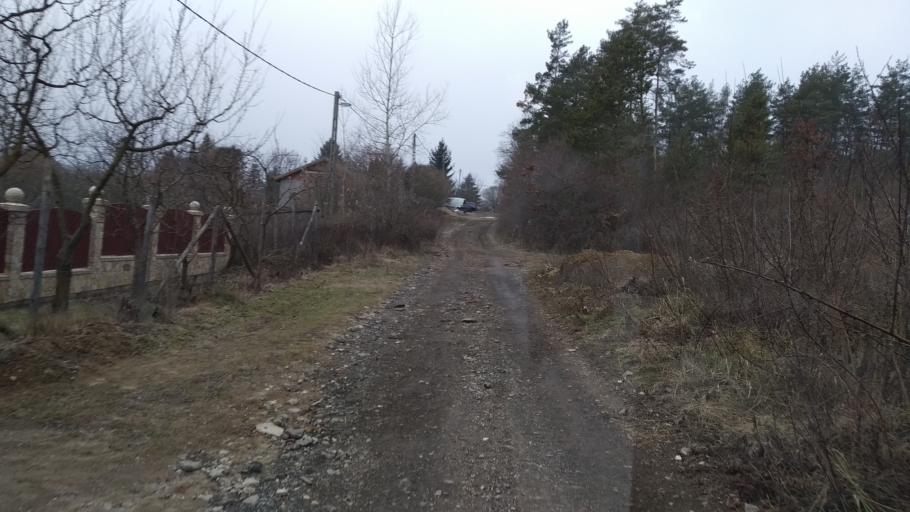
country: HU
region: Pest
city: Pilisborosjeno
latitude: 47.6067
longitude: 18.9620
